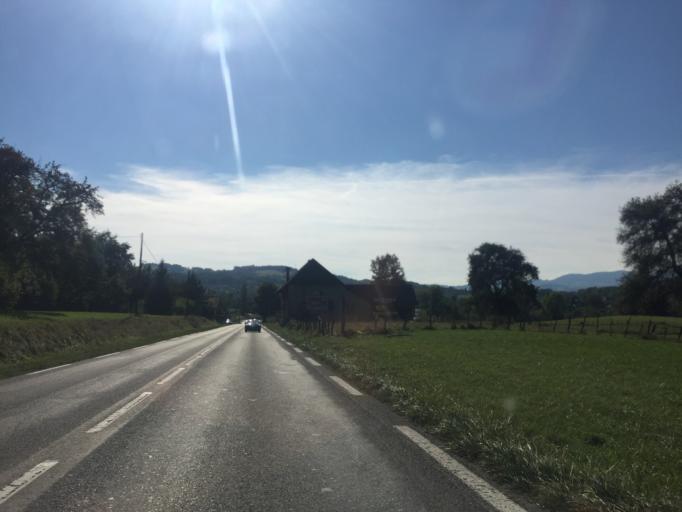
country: FR
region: Rhone-Alpes
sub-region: Departement de la Haute-Savoie
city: Alby-sur-Cheran
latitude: 45.8228
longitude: 6.0376
